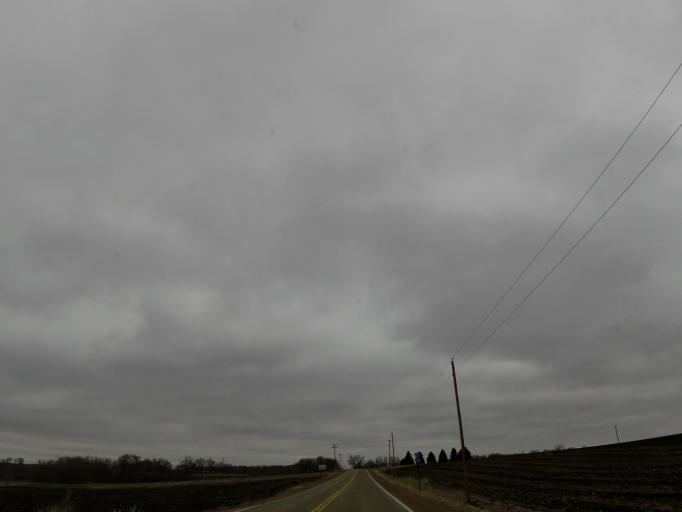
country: US
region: Minnesota
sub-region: Scott County
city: Shakopee
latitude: 44.7054
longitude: -93.5413
